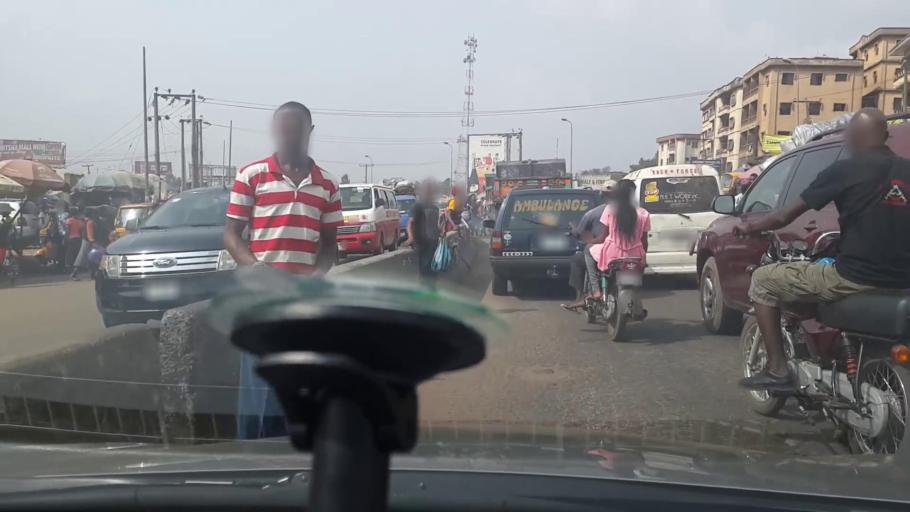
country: NG
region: Delta
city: Agbor
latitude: 6.2581
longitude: 6.1799
